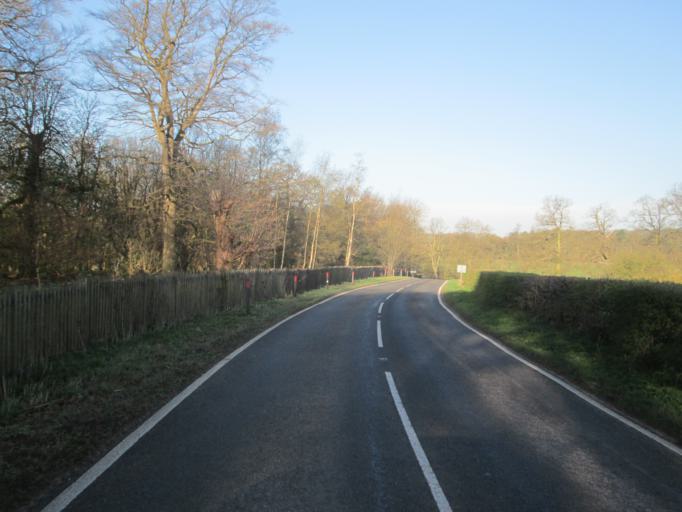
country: GB
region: England
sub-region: Derbyshire
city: Duffield
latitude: 52.9696
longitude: -1.5391
